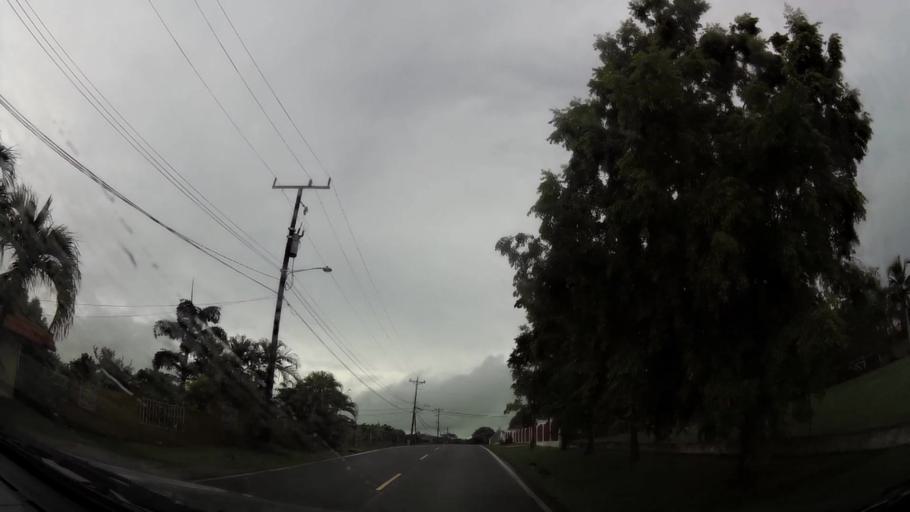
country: PA
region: Veraguas
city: Santiago de Veraguas
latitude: 8.0964
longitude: -80.9607
